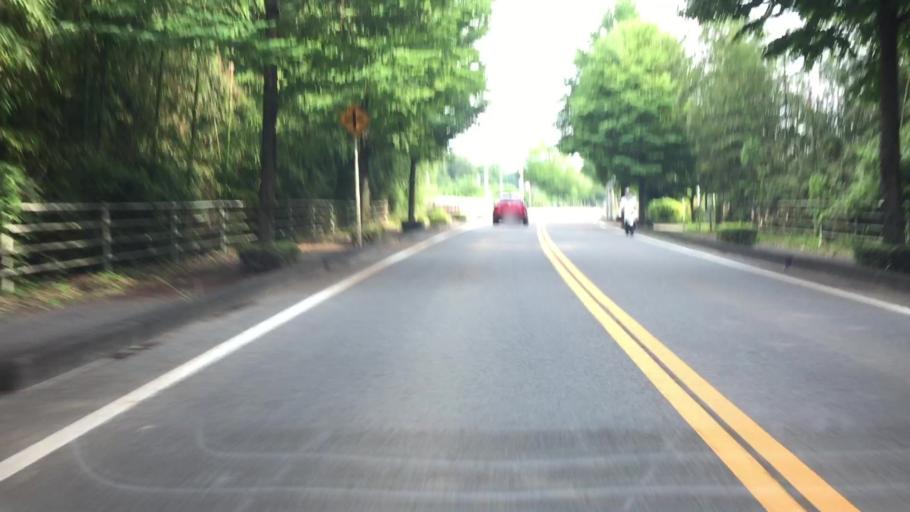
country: JP
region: Tochigi
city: Kuroiso
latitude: 36.9755
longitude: 139.9698
